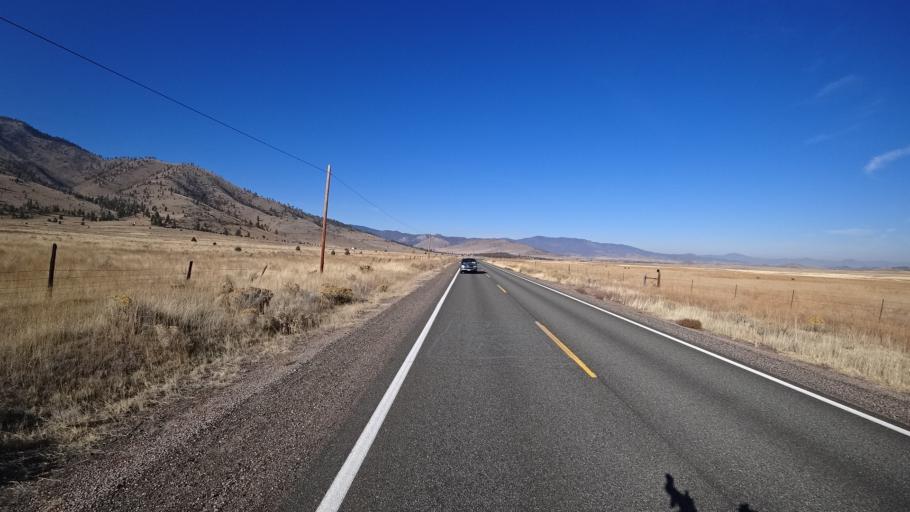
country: US
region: California
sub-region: Siskiyou County
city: Weed
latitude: 41.4783
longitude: -122.4909
